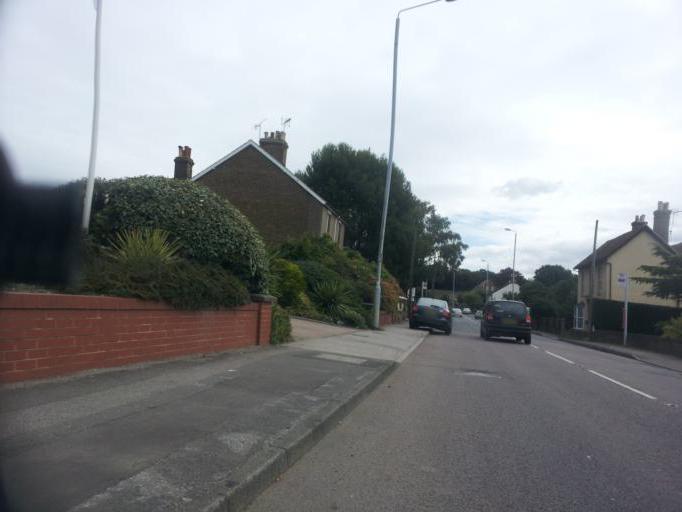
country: GB
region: England
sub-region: Kent
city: Newington
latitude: 51.3489
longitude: 0.6838
